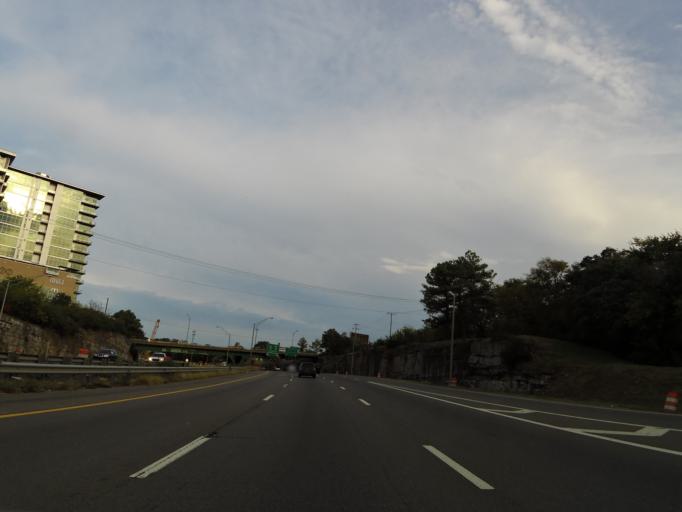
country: US
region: Tennessee
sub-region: Davidson County
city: Nashville
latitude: 36.1511
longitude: -86.7862
